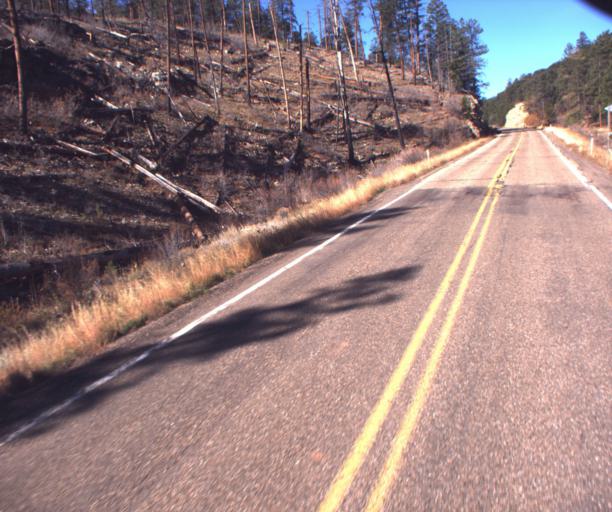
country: US
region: Arizona
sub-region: Coconino County
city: Fredonia
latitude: 36.7312
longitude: -112.1542
